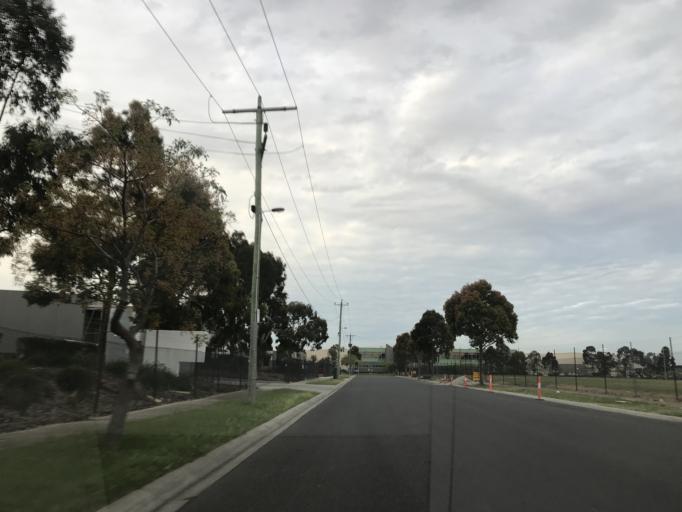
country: AU
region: Victoria
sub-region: Brimbank
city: Derrimut
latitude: -37.8069
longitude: 144.7816
